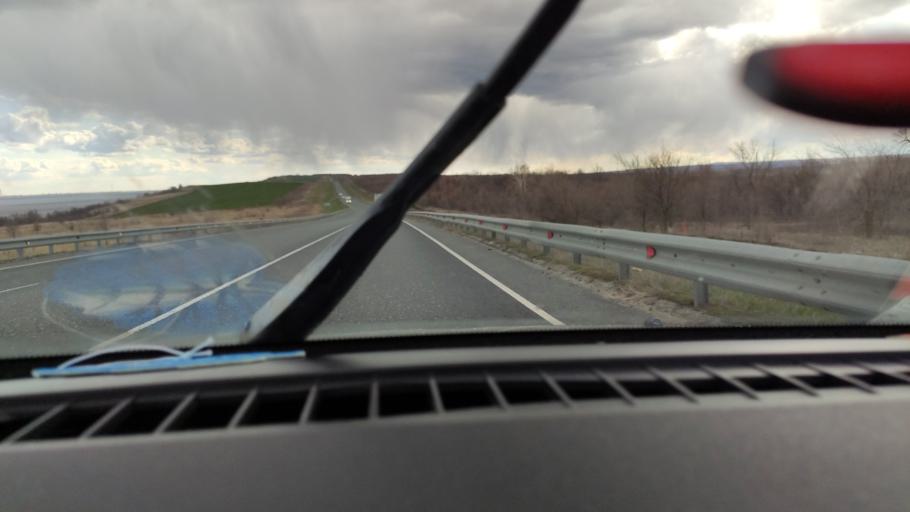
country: RU
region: Saratov
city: Balakovo
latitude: 52.1971
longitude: 47.8608
